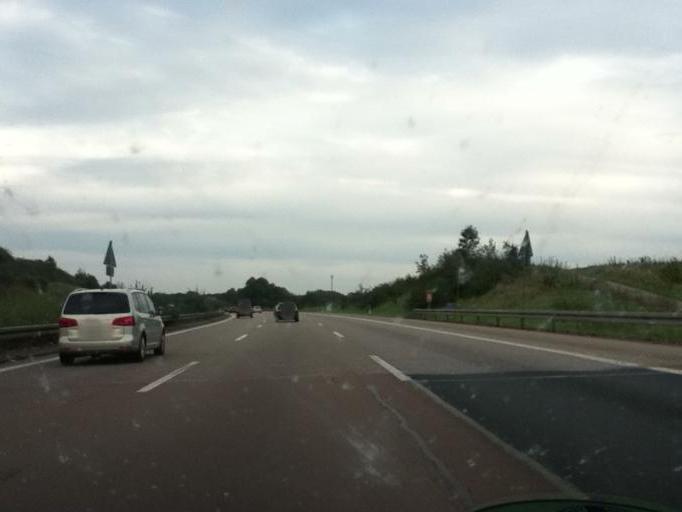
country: DE
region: Saxony
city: Reinsberg
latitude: 51.0579
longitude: 13.4316
